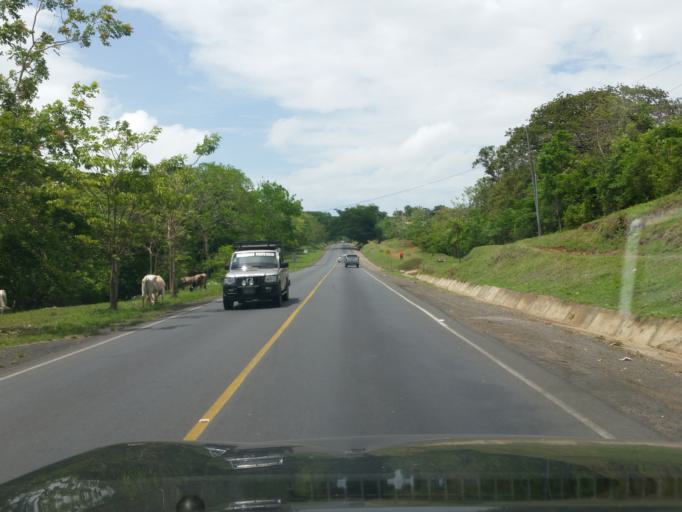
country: NI
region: Masaya
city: Masaya
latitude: 11.9420
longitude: -86.0911
